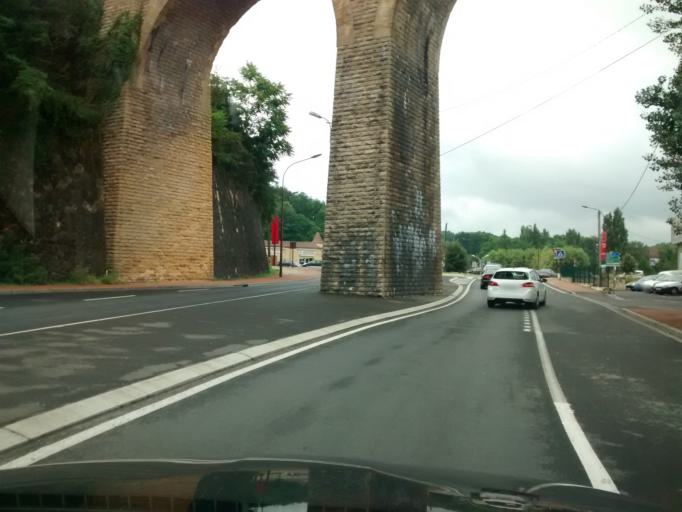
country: FR
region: Aquitaine
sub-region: Departement de la Dordogne
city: Sarlat-la-Caneda
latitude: 44.8781
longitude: 1.2173
